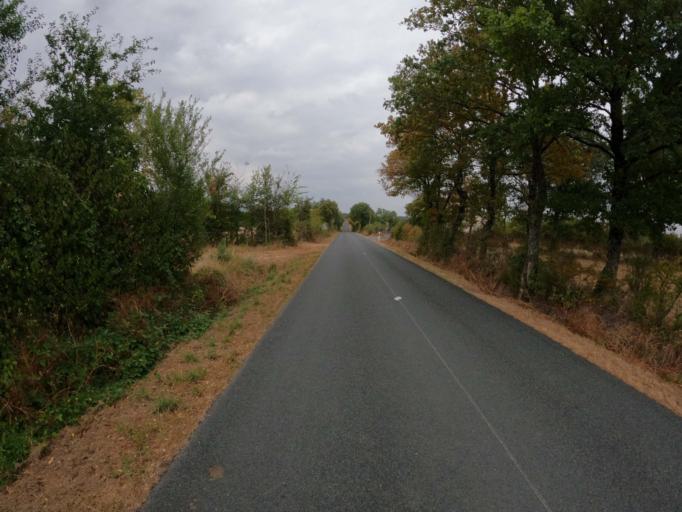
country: FR
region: Pays de la Loire
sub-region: Departement de la Vendee
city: Tiffauges
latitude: 46.9975
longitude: -1.1084
